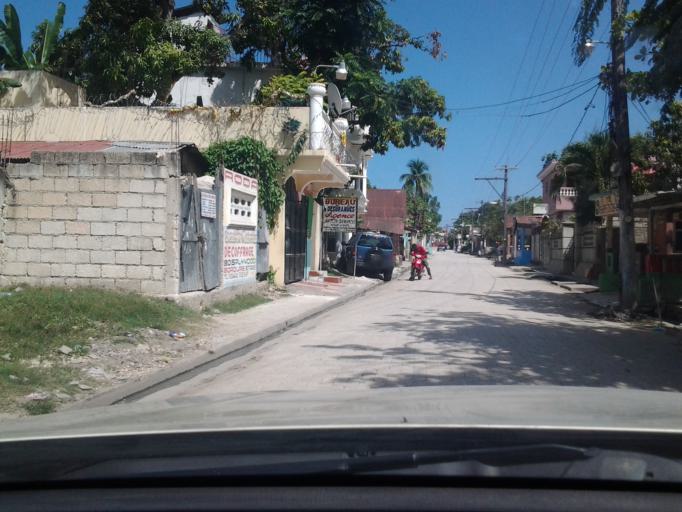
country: HT
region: Ouest
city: Tigwav
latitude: 18.4286
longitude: -72.8700
